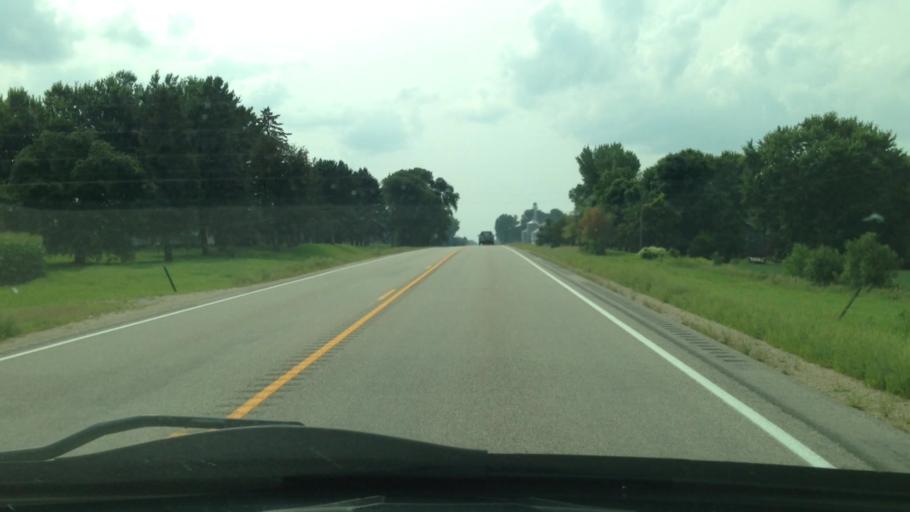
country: US
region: Minnesota
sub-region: Wabasha County
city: Elgin
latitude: 44.1658
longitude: -92.3900
